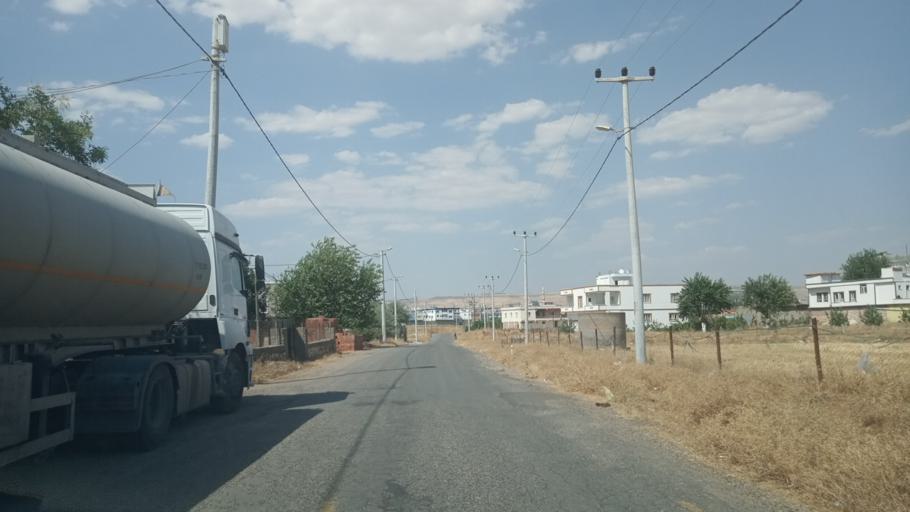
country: TR
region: Batman
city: Binatli
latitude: 37.8419
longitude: 41.2115
